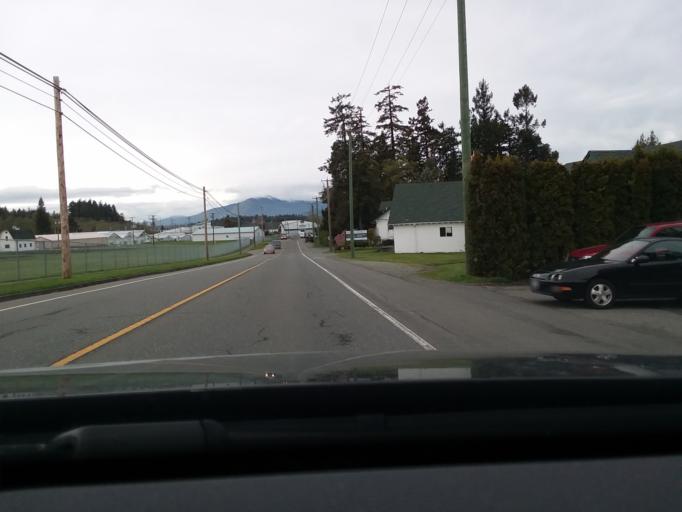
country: CA
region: British Columbia
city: North Saanich
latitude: 48.6200
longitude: -123.4169
